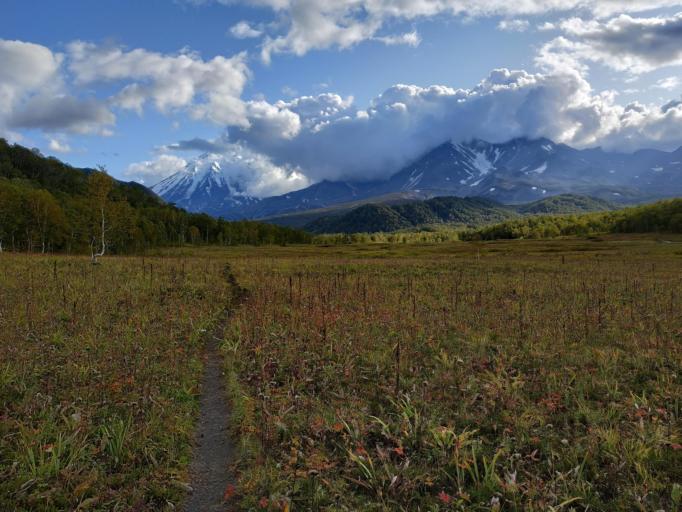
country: RU
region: Kamtsjatka
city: Petropavlovsk-Kamchatsky
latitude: 53.4699
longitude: 158.7293
